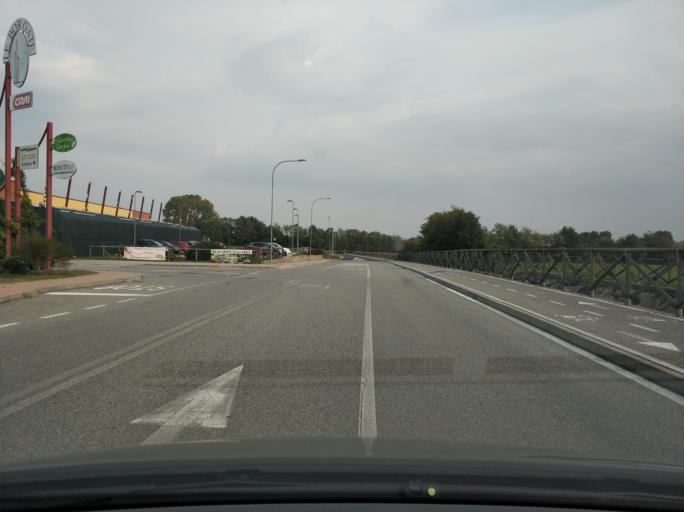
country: IT
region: Piedmont
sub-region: Provincia di Torino
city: San Francesco al Campo
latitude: 45.2340
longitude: 7.6518
